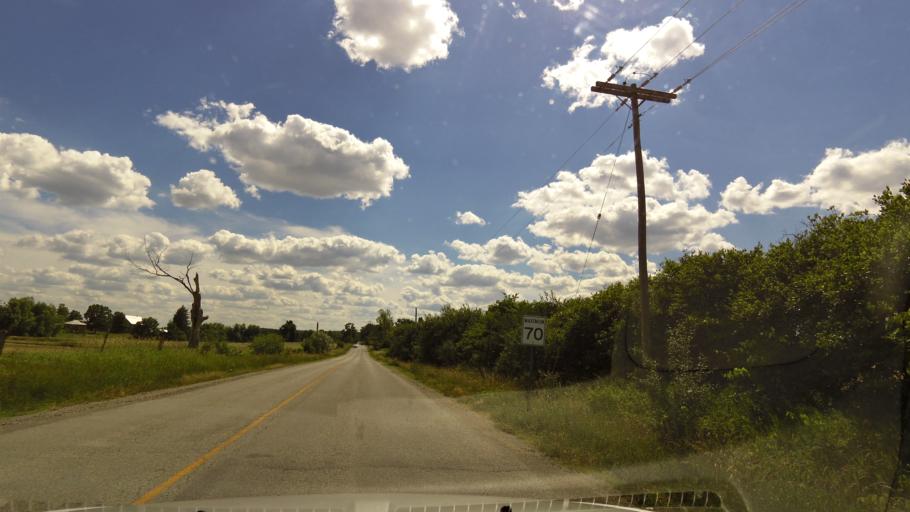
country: CA
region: Ontario
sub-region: Halton
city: Milton
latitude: 43.5788
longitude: -79.9272
